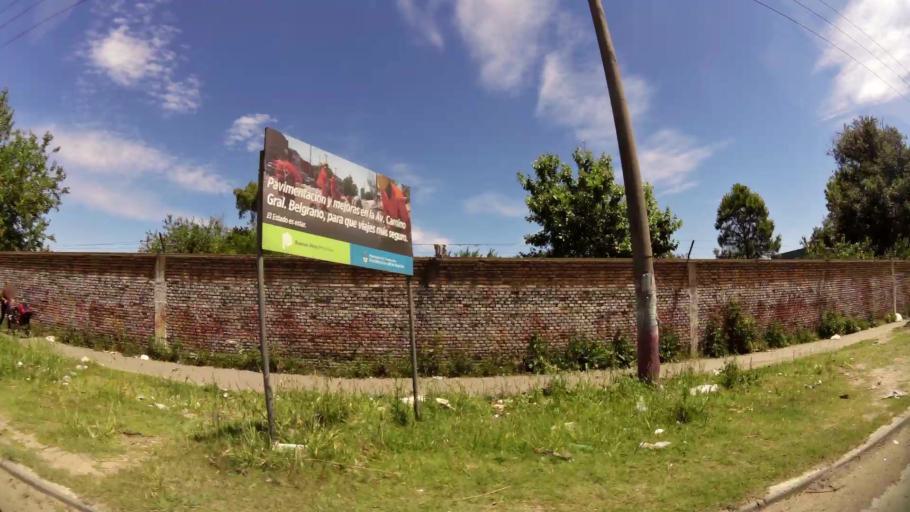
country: AR
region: Buenos Aires
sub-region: Partido de Lanus
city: Lanus
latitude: -34.7315
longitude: -58.3274
